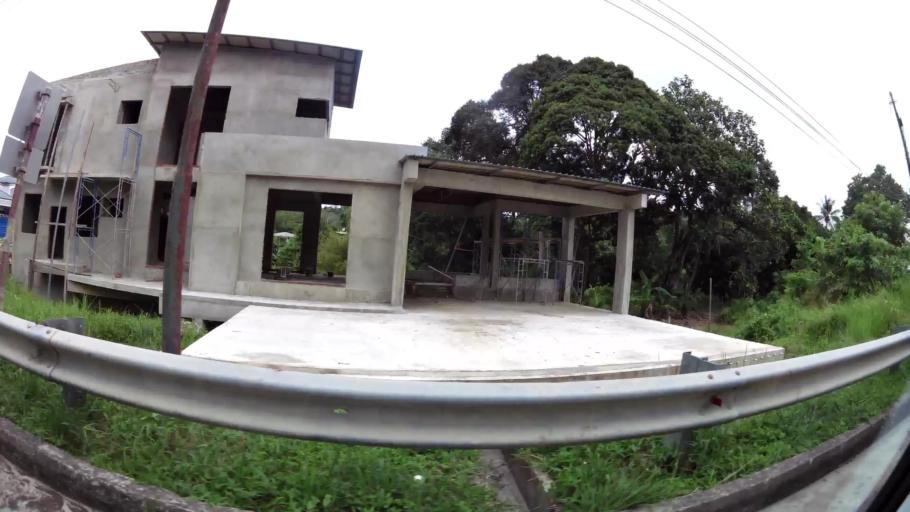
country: BN
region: Brunei and Muara
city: Bandar Seri Begawan
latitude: 4.8878
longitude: 114.9031
